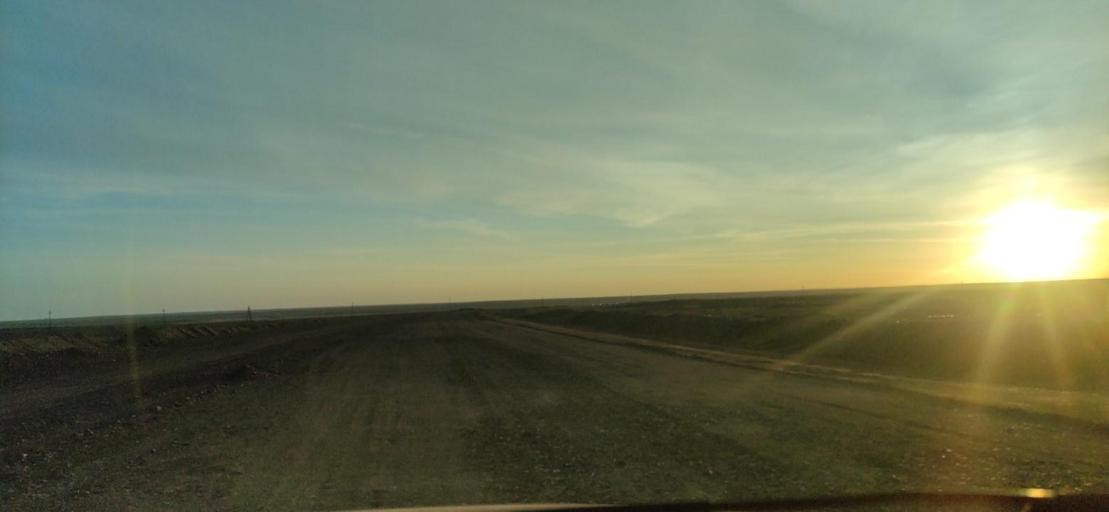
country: KZ
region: Qaraghandy
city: Saryshaghan
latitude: 46.0113
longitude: 73.5876
